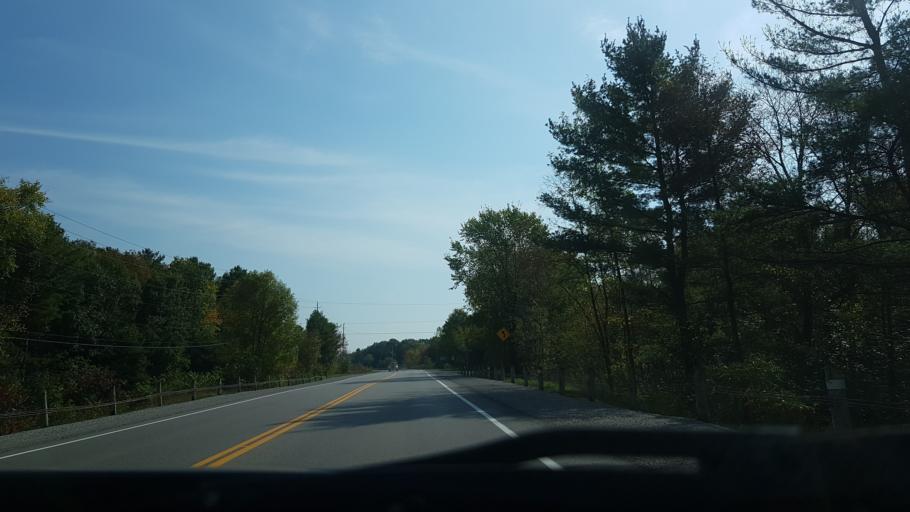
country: CA
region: Ontario
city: Orillia
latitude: 44.7447
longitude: -79.3189
